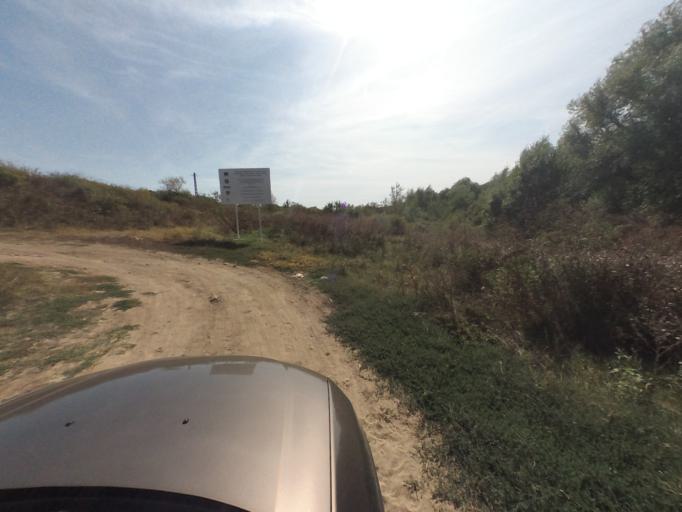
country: RO
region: Vaslui
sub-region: Comuna Costesti
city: Costesti
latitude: 46.5142
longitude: 27.7436
